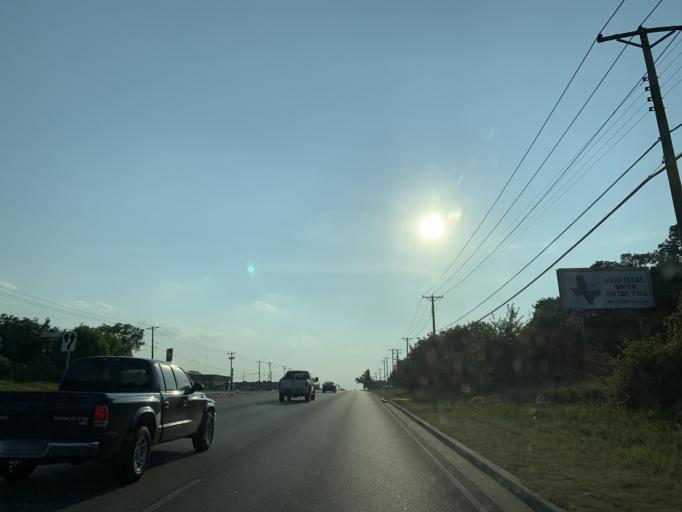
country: US
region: Texas
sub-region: Tarrant County
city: Hurst
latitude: 32.8092
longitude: -97.1807
